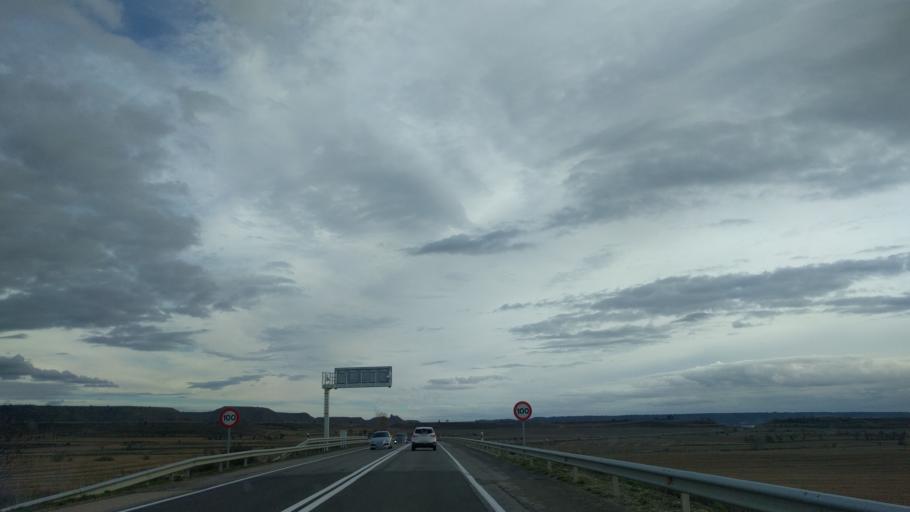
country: ES
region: Aragon
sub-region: Provincia de Huesca
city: Huesca
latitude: 42.1604
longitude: -0.4113
